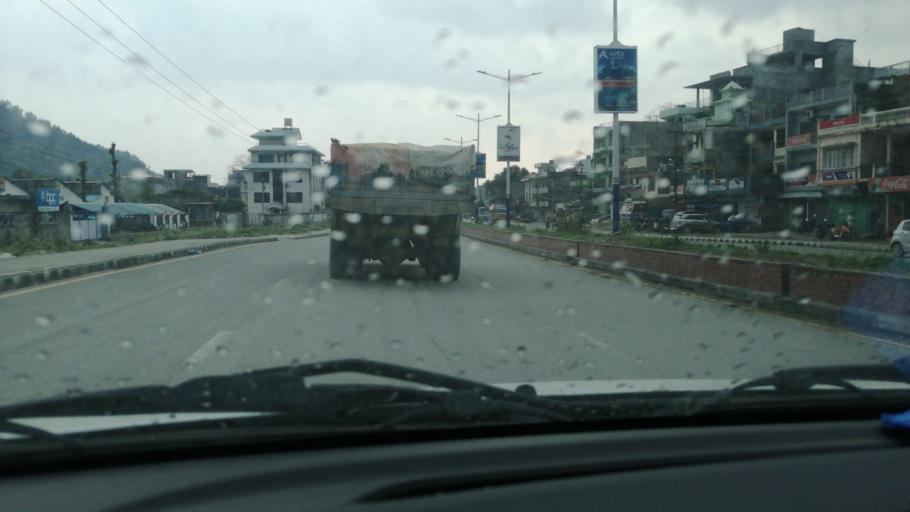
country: NP
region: Western Region
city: Butwal
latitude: 27.7086
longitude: 83.4678
